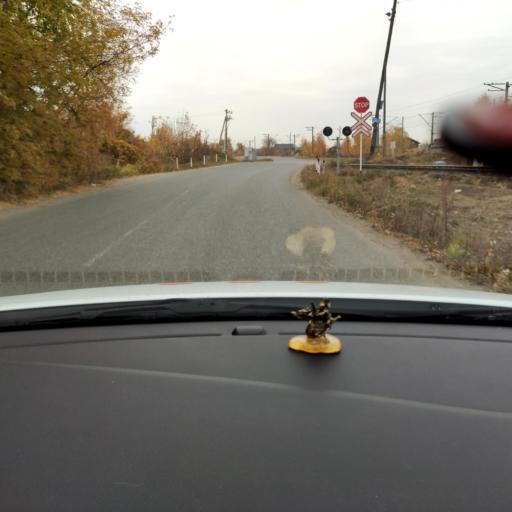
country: RU
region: Tatarstan
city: Verkhniy Uslon
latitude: 55.8018
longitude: 49.0227
